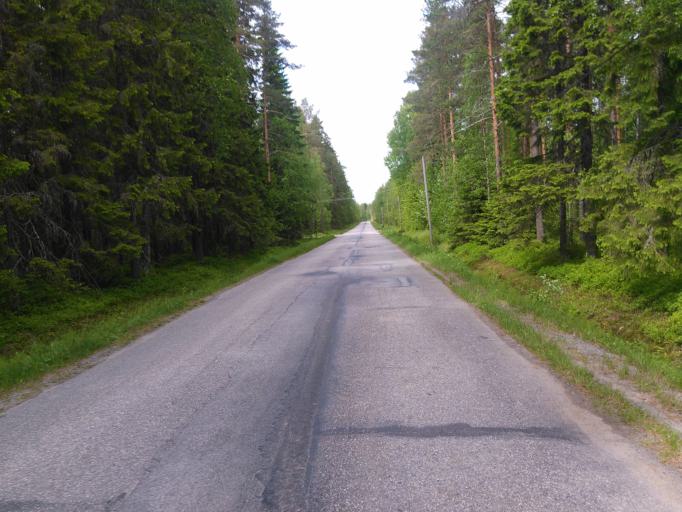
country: SE
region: Vaesterbotten
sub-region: Umea Kommun
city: Ersmark
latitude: 63.8706
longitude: 20.3324
